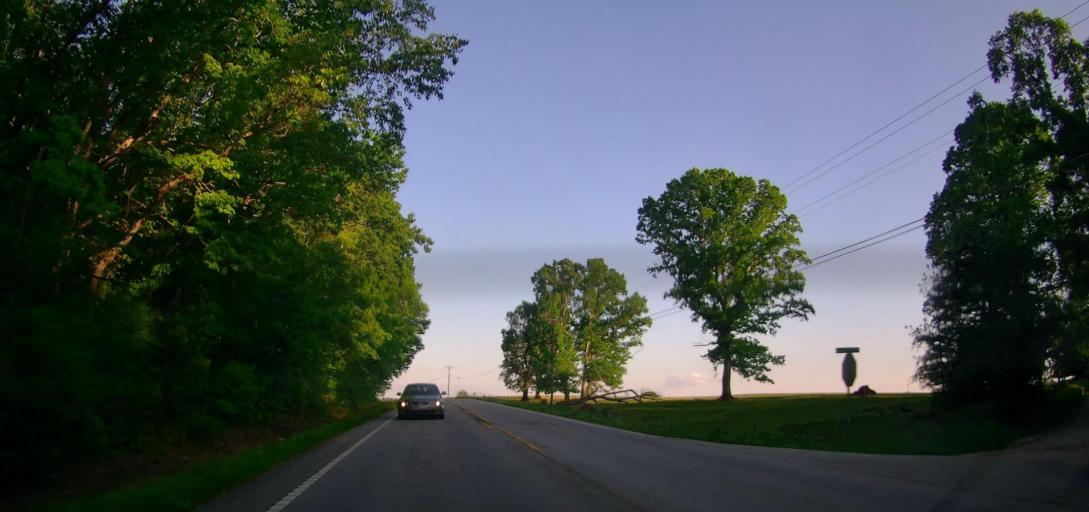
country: US
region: Georgia
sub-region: Walton County
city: Social Circle
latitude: 33.5384
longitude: -83.7243
